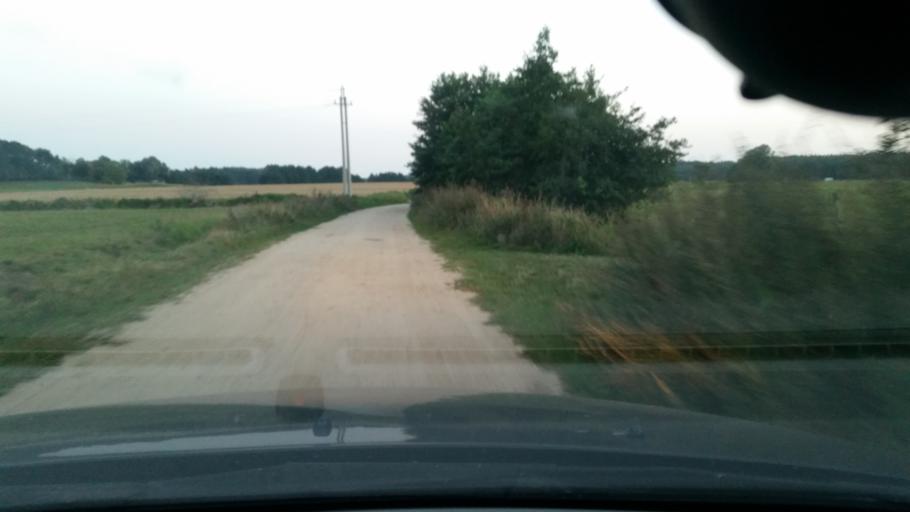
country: PL
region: Pomeranian Voivodeship
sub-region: Powiat wejherowski
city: Choczewo
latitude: 54.7768
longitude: 17.7917
